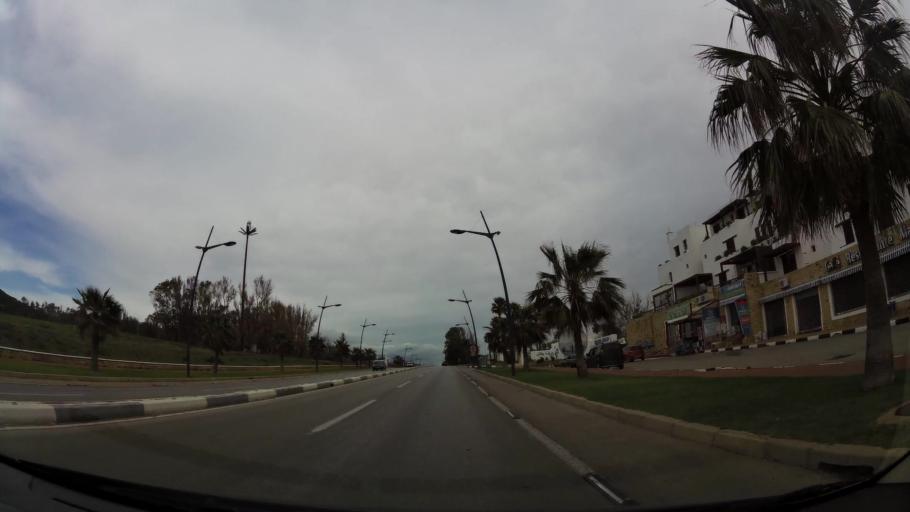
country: ES
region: Ceuta
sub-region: Ceuta
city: Ceuta
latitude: 35.7597
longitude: -5.3482
